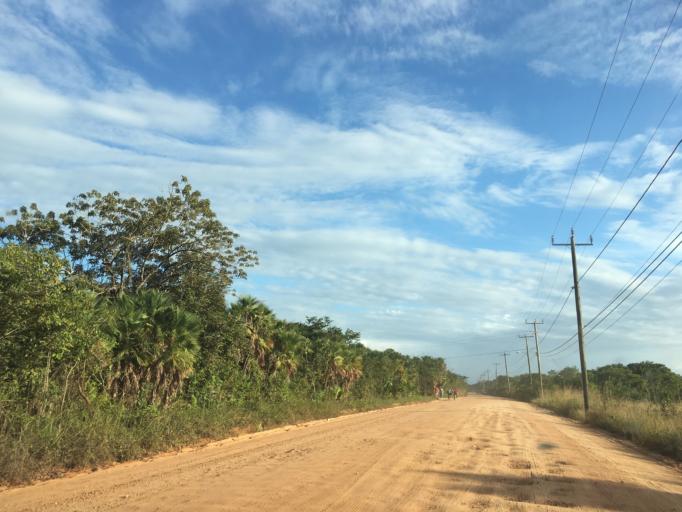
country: BZ
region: Stann Creek
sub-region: Dangriga
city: Dangriga
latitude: 16.8464
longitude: -88.2780
